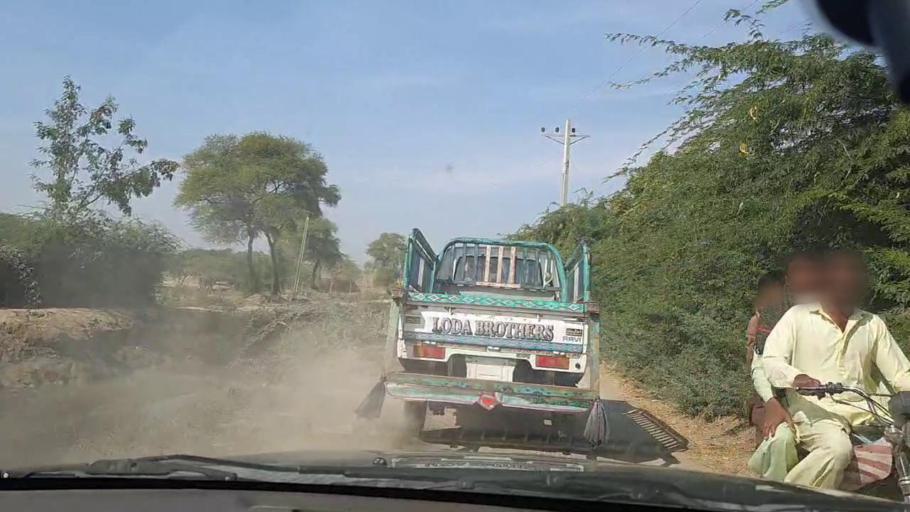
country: PK
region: Sindh
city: Mirpur Batoro
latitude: 24.7347
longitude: 68.2572
